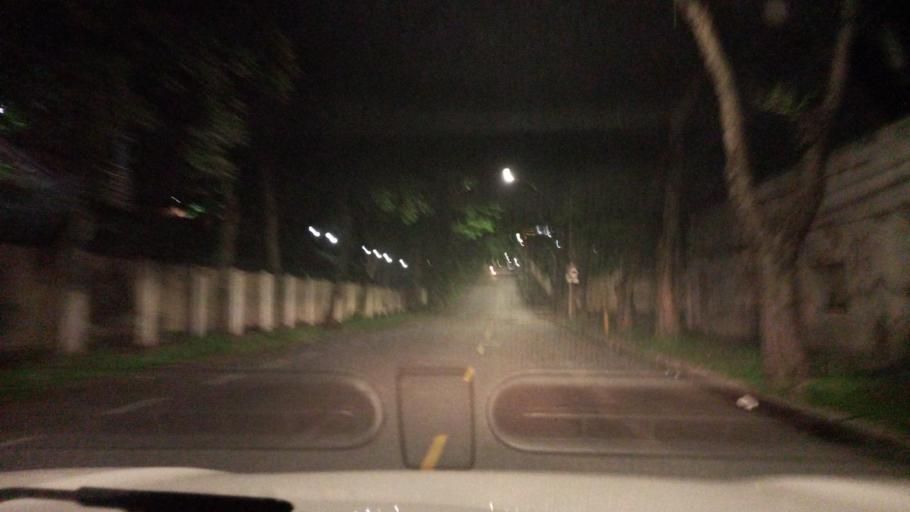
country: BR
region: Minas Gerais
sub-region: Belo Horizonte
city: Belo Horizonte
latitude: -19.8577
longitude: -43.9203
